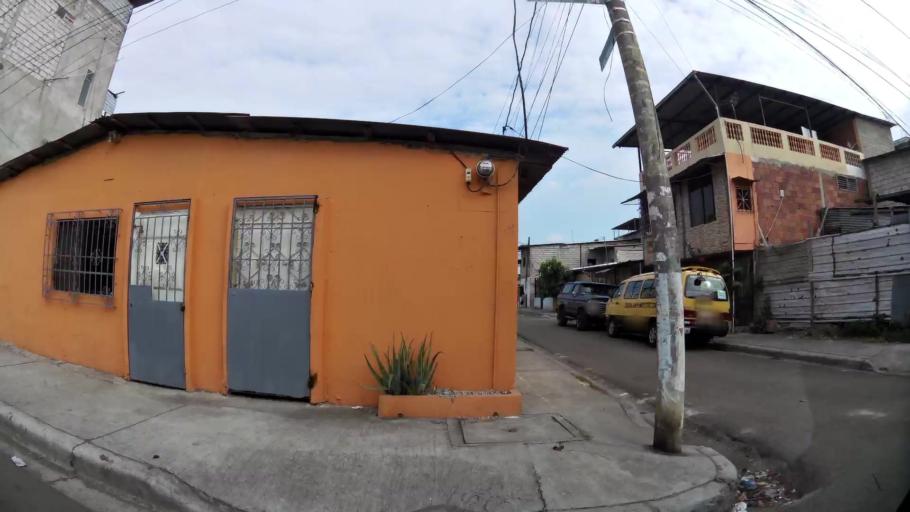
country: EC
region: Guayas
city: Guayaquil
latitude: -2.2565
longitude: -79.8871
